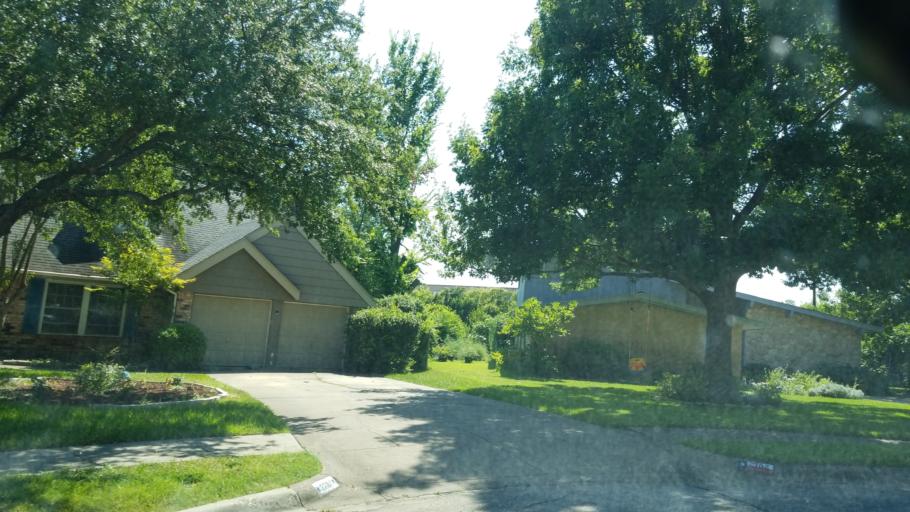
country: US
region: Texas
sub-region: Dallas County
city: Farmers Branch
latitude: 32.9142
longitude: -96.8855
